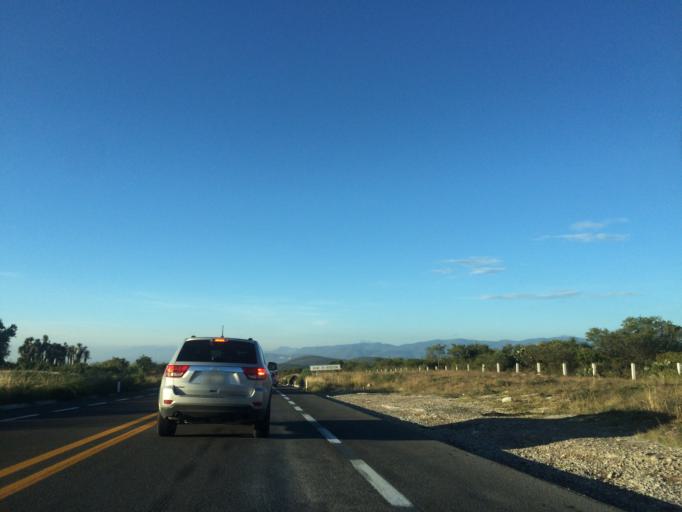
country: MX
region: Puebla
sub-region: Tehuacan
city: Magdalena Cuayucatepec
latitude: 18.6033
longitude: -97.4748
